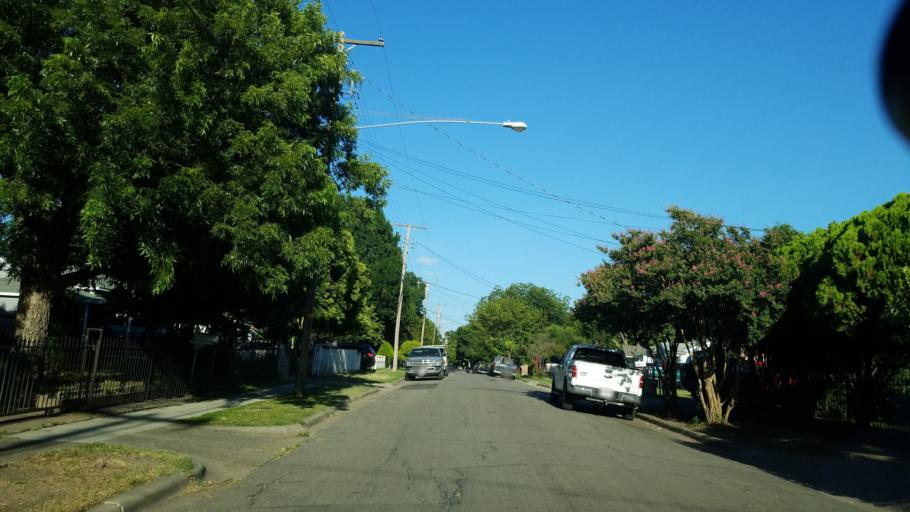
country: US
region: Texas
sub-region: Dallas County
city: Dallas
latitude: 32.7757
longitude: -96.7093
